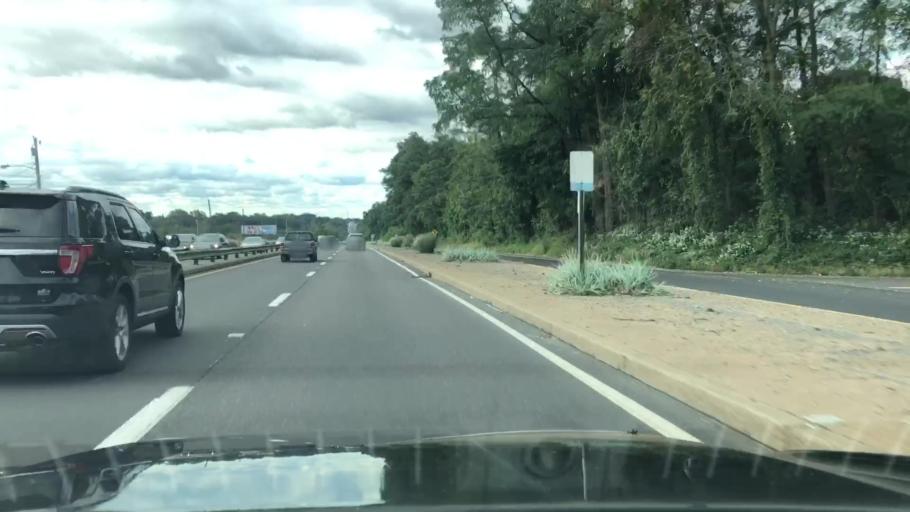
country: US
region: Pennsylvania
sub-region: Bucks County
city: Penndel
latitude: 40.1562
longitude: -74.9435
